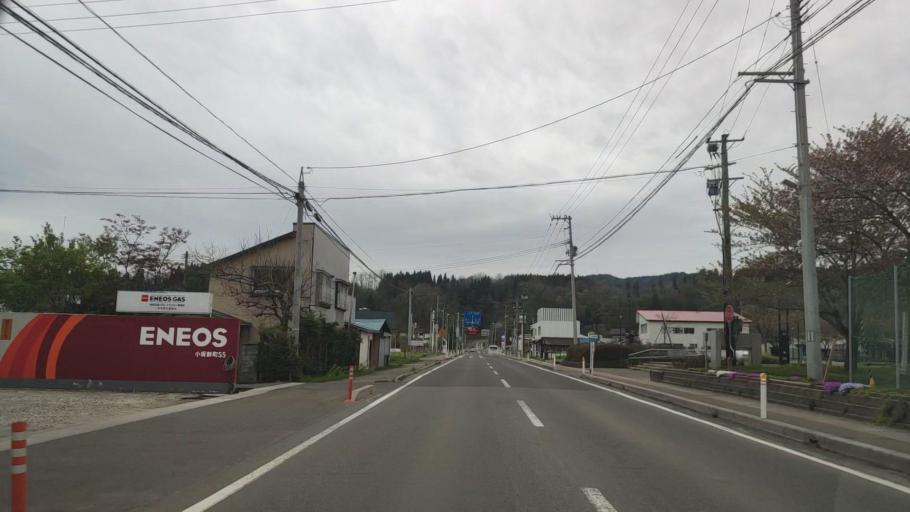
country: JP
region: Akita
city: Hanawa
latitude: 40.3246
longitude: 140.7436
